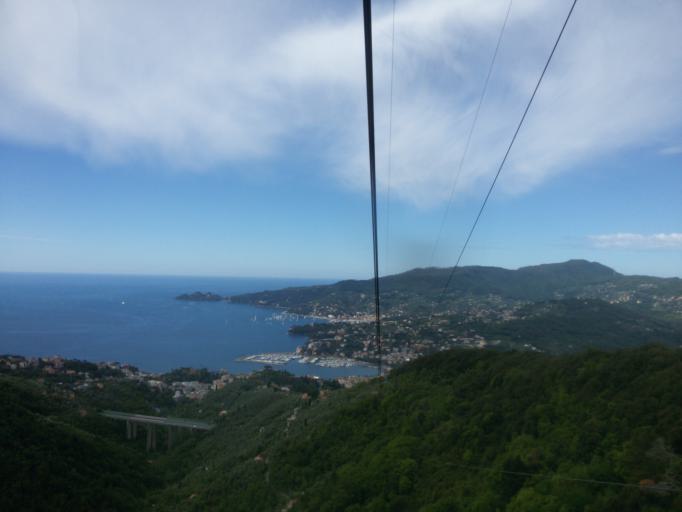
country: IT
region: Liguria
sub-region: Provincia di Genova
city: Rapallo
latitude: 44.3632
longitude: 9.2475
